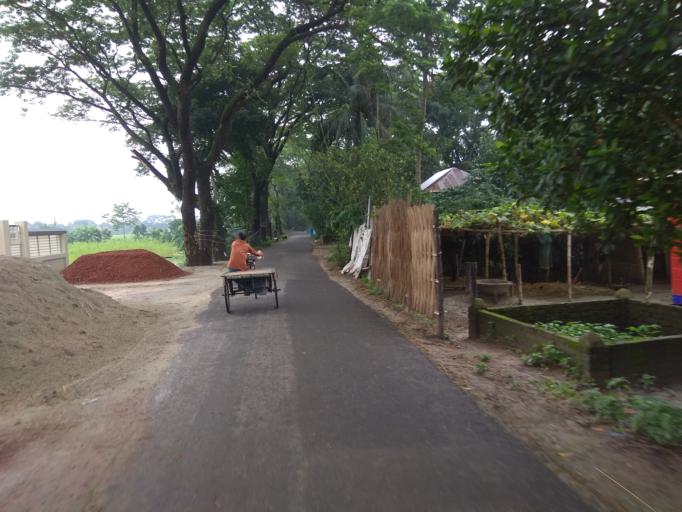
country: BD
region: Dhaka
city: Dohar
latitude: 23.4721
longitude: 90.0700
